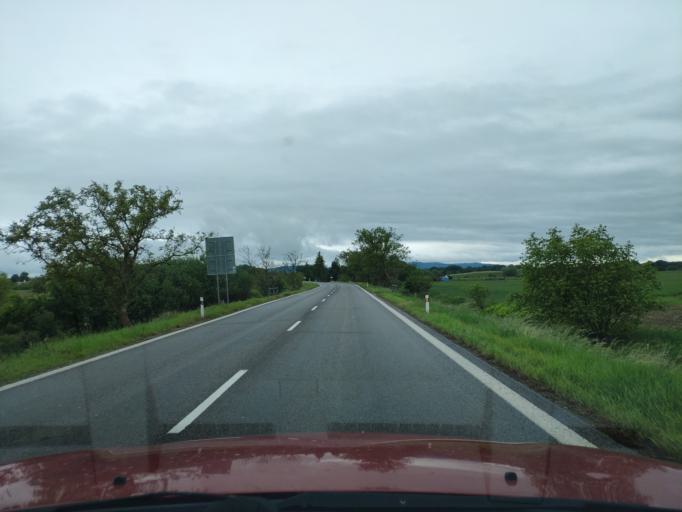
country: HU
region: Borsod-Abauj-Zemplen
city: Karcsa
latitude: 48.4344
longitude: 21.8734
